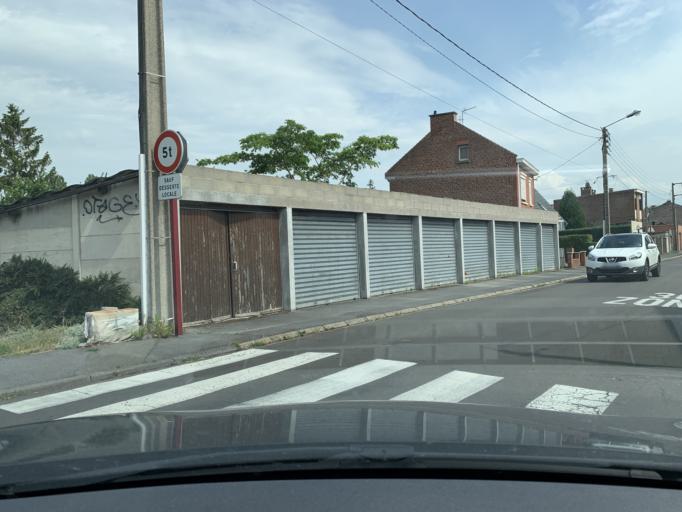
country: FR
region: Nord-Pas-de-Calais
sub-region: Departement du Nord
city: Douai
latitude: 50.3627
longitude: 3.0673
